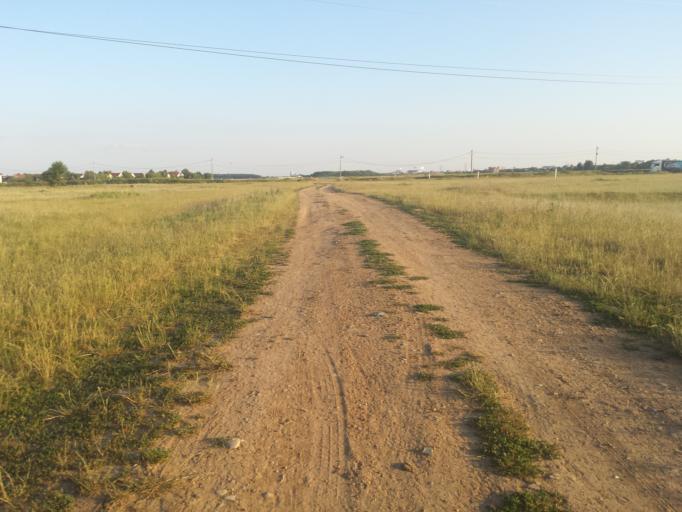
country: RO
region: Ilfov
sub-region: Comuna Tunari
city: Tunari
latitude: 44.5167
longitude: 26.1528
